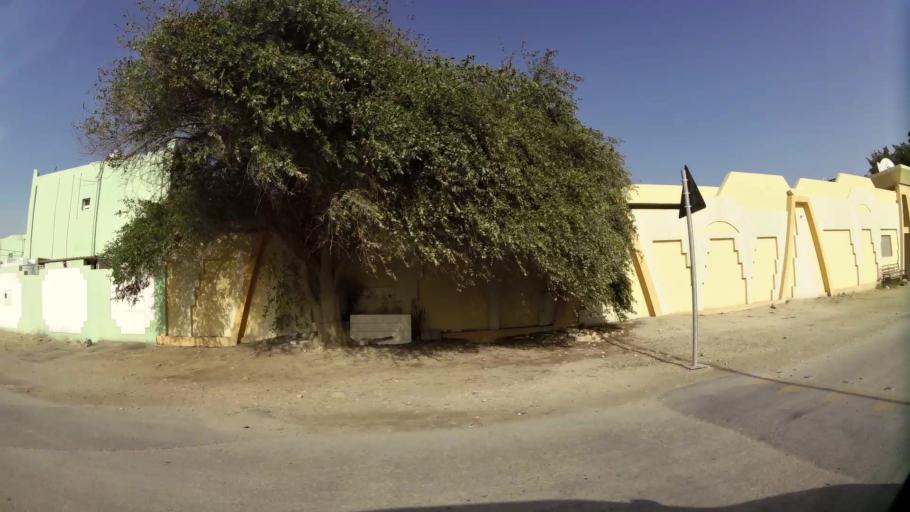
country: QA
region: Baladiyat ar Rayyan
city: Ar Rayyan
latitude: 25.3416
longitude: 51.4435
